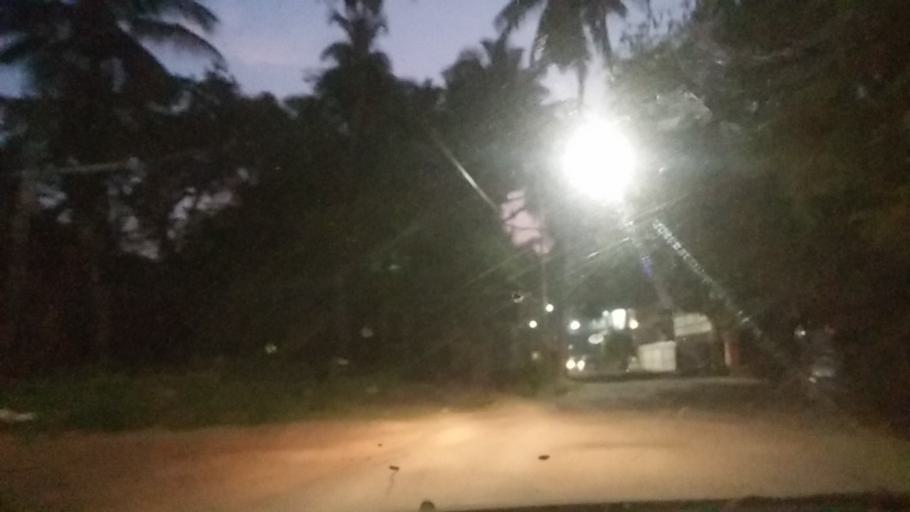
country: IN
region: Goa
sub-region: South Goa
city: Madgaon
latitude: 15.2623
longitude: 73.9646
